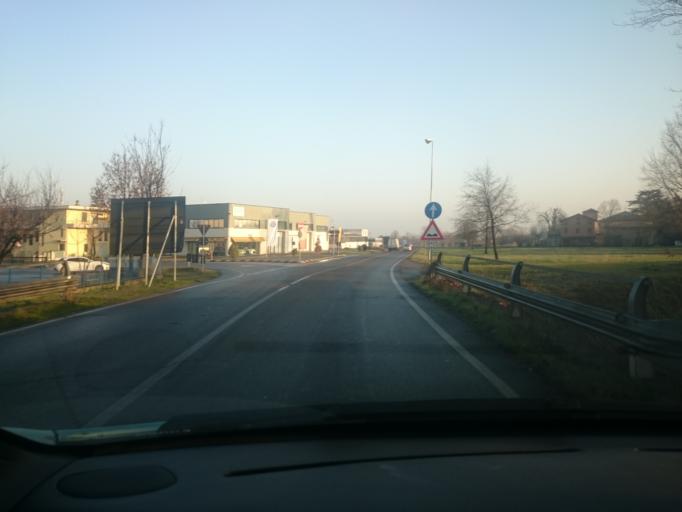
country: IT
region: Emilia-Romagna
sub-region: Provincia di Reggio Emilia
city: Scandiano
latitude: 44.6011
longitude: 10.7039
